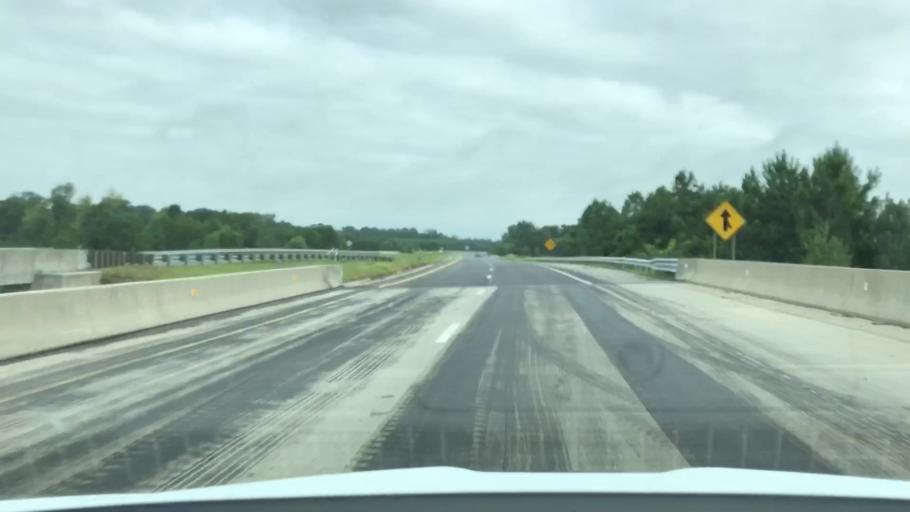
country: US
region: North Carolina
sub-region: Wilson County
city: Lucama
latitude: 35.6671
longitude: -77.9564
